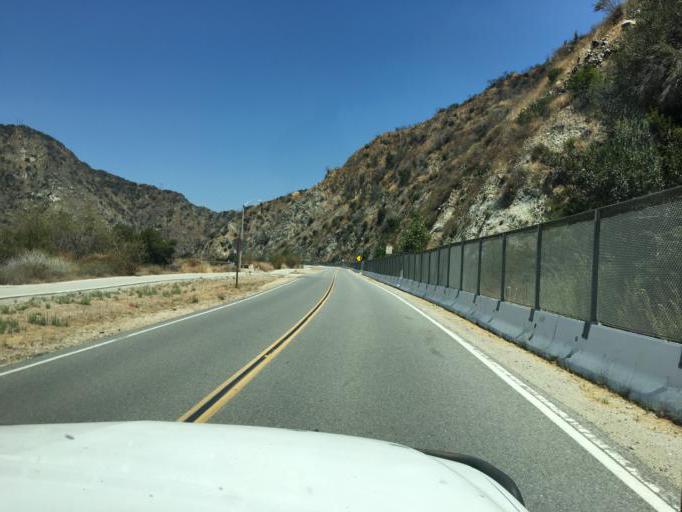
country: US
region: California
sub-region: Los Angeles County
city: Azusa
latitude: 34.1592
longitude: -117.9010
